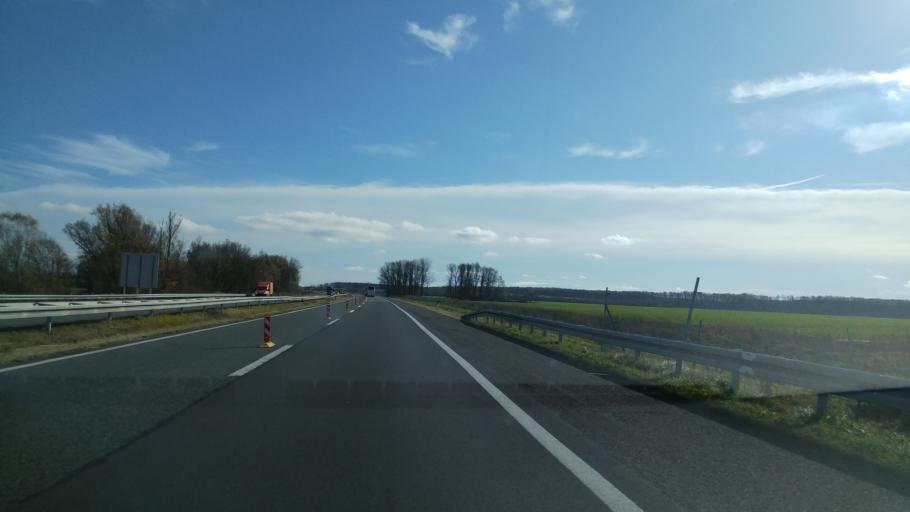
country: HR
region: Sisacko-Moslavacka
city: Lipovljani
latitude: 45.3809
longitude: 16.8733
